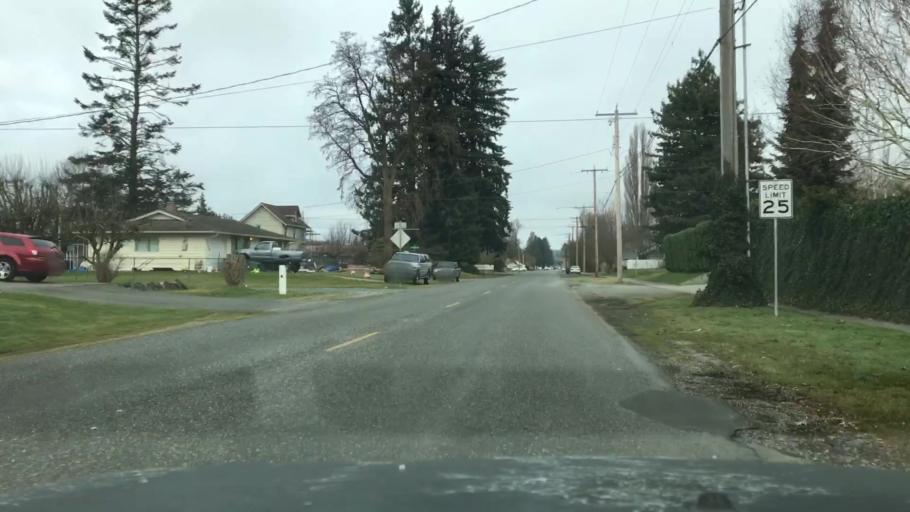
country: US
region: Washington
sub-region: Skagit County
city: Sedro-Woolley
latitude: 48.4936
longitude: -122.2260
